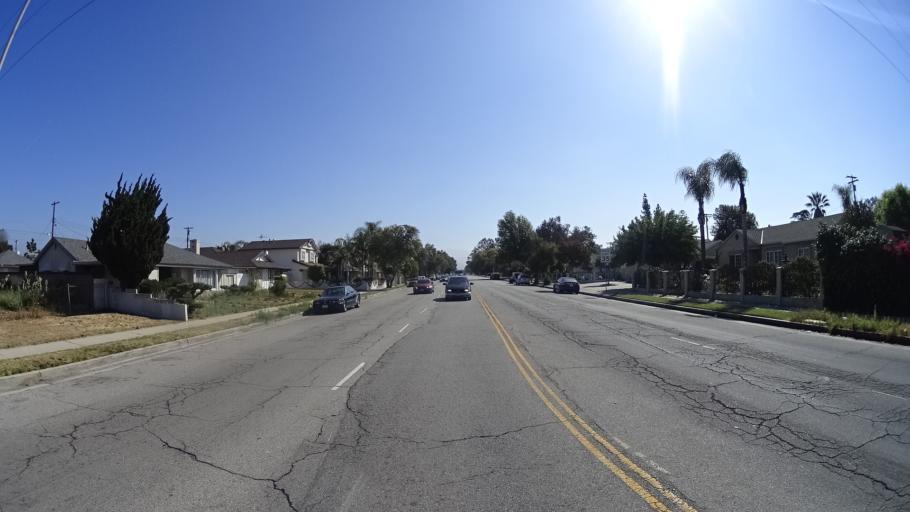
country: US
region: California
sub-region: Los Angeles County
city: Van Nuys
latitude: 34.2316
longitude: -118.4261
